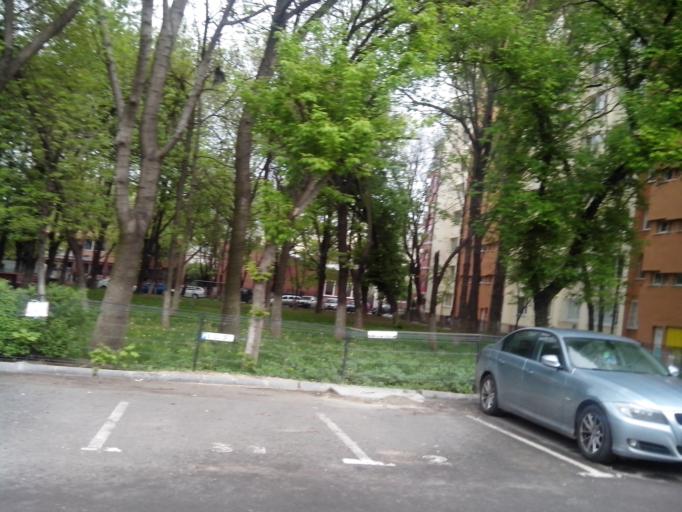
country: RO
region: Bucuresti
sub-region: Municipiul Bucuresti
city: Bucuresti
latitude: 44.4228
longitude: 26.1044
